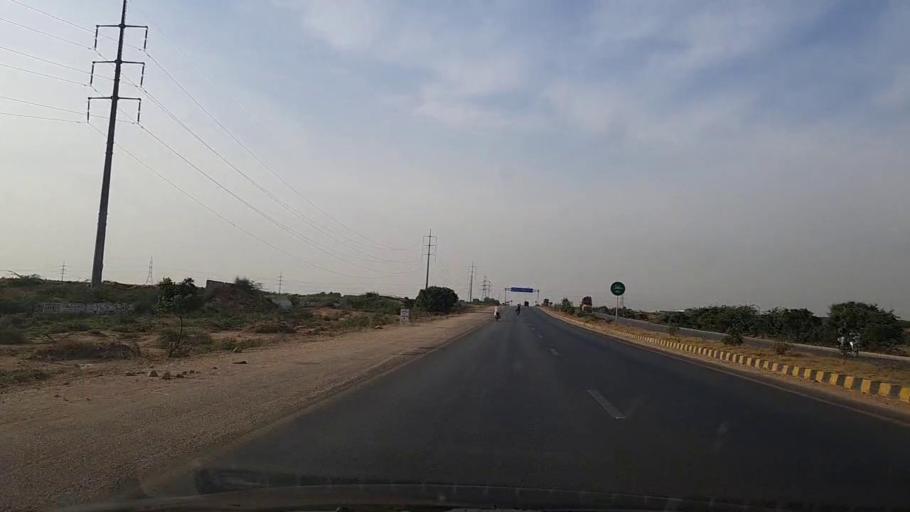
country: PK
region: Sindh
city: Gharo
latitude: 24.7631
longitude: 67.5551
